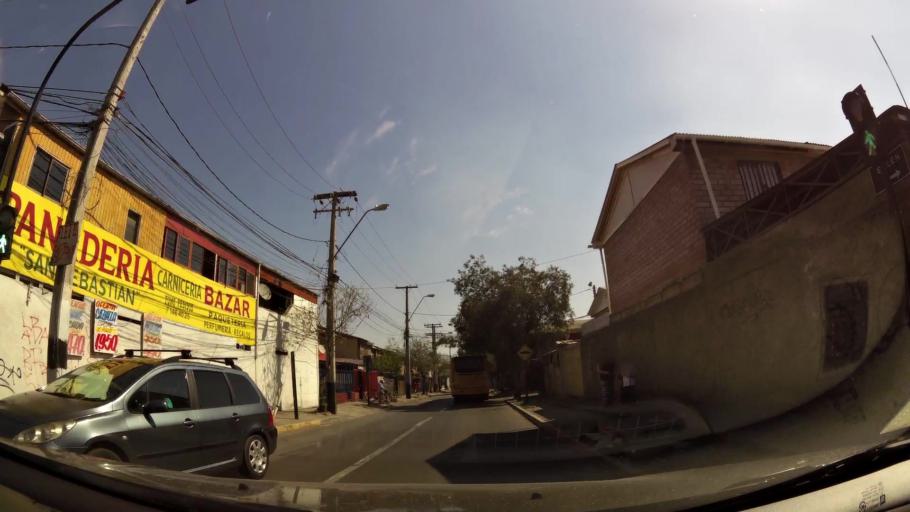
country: CL
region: Santiago Metropolitan
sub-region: Provincia de Cordillera
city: Puente Alto
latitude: -33.6290
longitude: -70.6121
